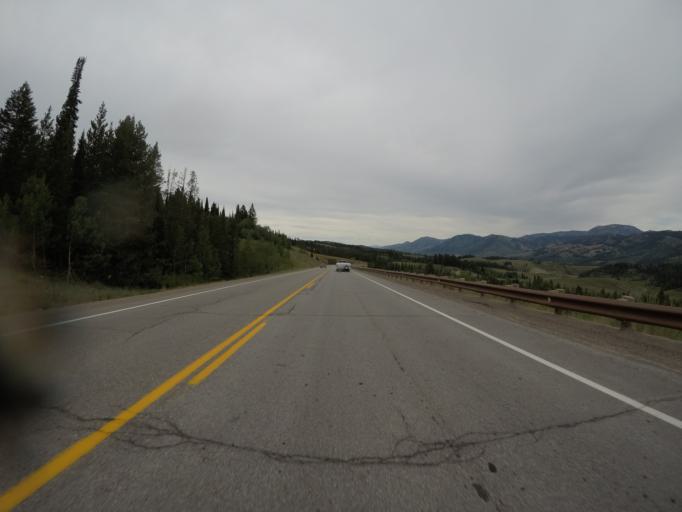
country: US
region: Wyoming
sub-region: Lincoln County
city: Afton
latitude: 42.5090
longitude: -110.9091
